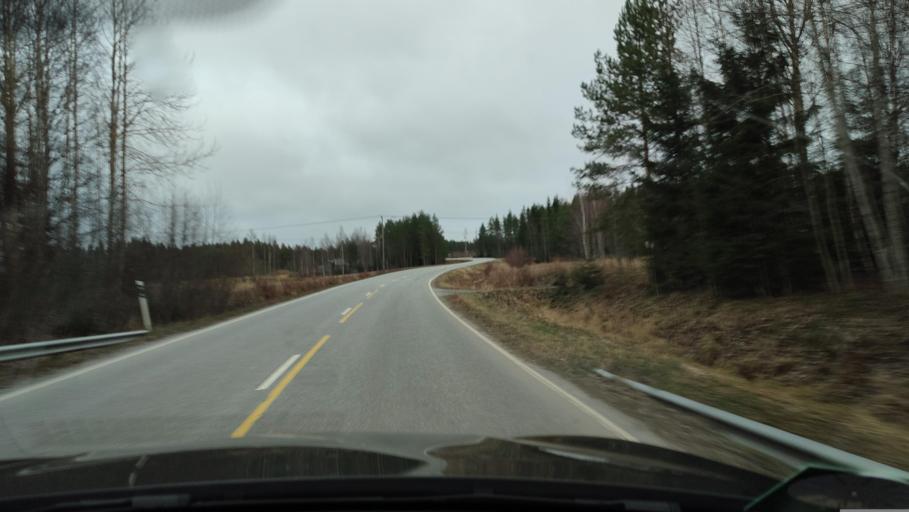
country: FI
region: Southern Ostrobothnia
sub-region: Suupohja
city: Karijoki
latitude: 62.2351
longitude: 21.7504
